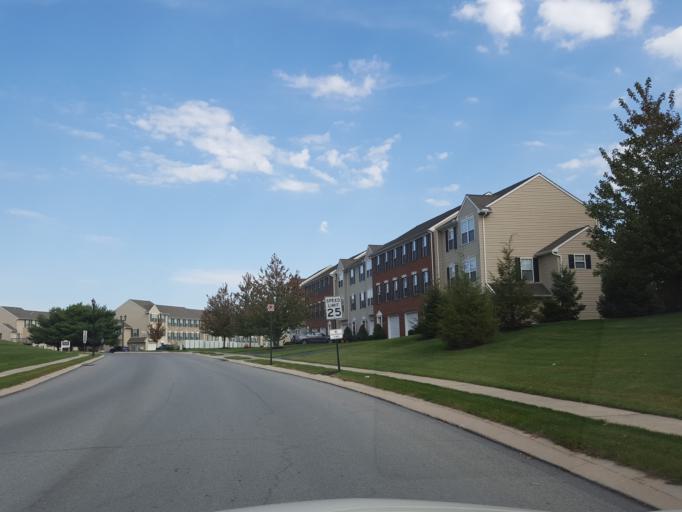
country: US
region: Pennsylvania
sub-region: York County
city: Yoe
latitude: 39.9185
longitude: -76.6259
